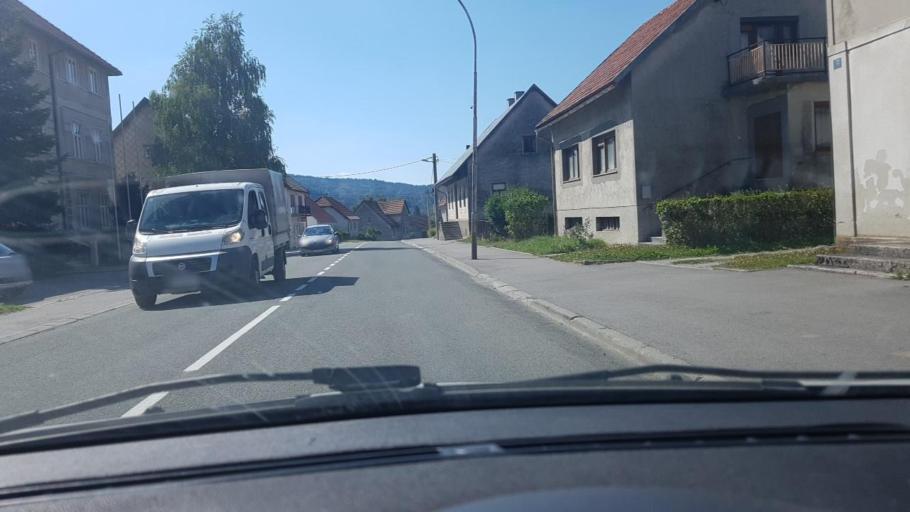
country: SI
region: Kostel
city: Kostel
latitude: 45.3733
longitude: 14.9358
